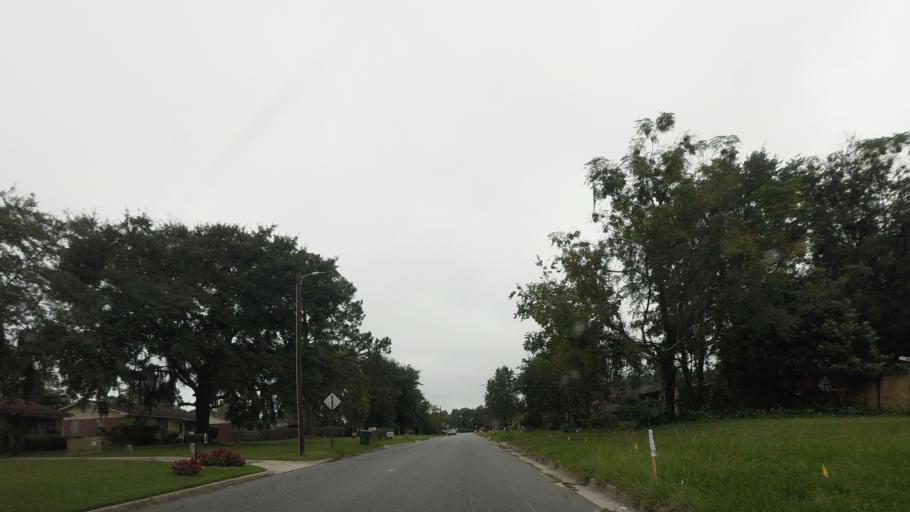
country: US
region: Georgia
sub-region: Lowndes County
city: Valdosta
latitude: 30.8186
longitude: -83.2762
